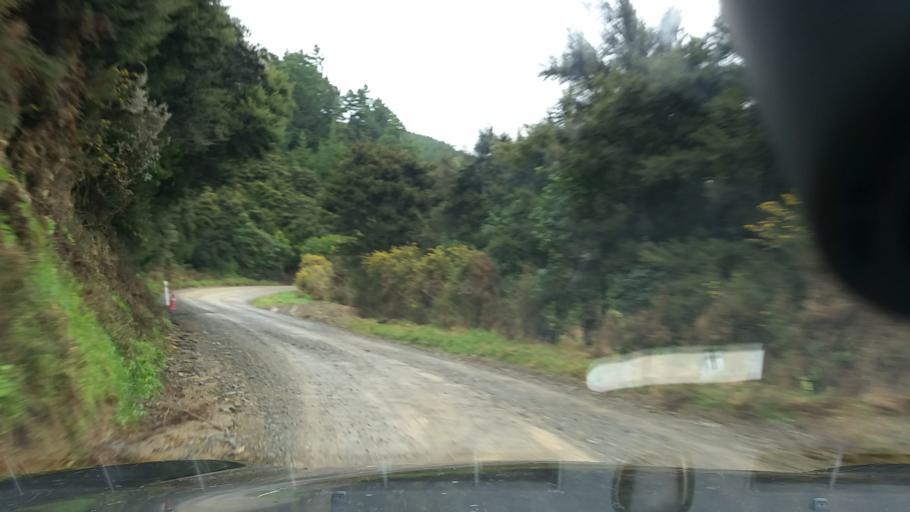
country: NZ
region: Marlborough
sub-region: Marlborough District
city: Picton
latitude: -41.3597
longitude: 174.0699
